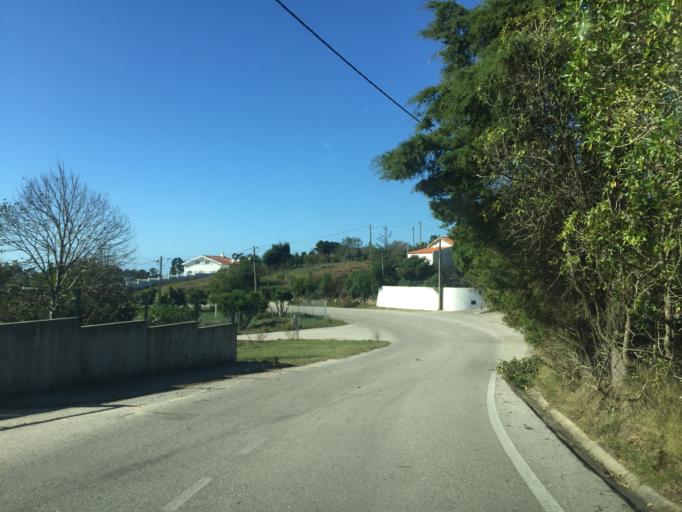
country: PT
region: Coimbra
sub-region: Figueira da Foz
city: Tavarede
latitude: 40.1880
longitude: -8.8349
